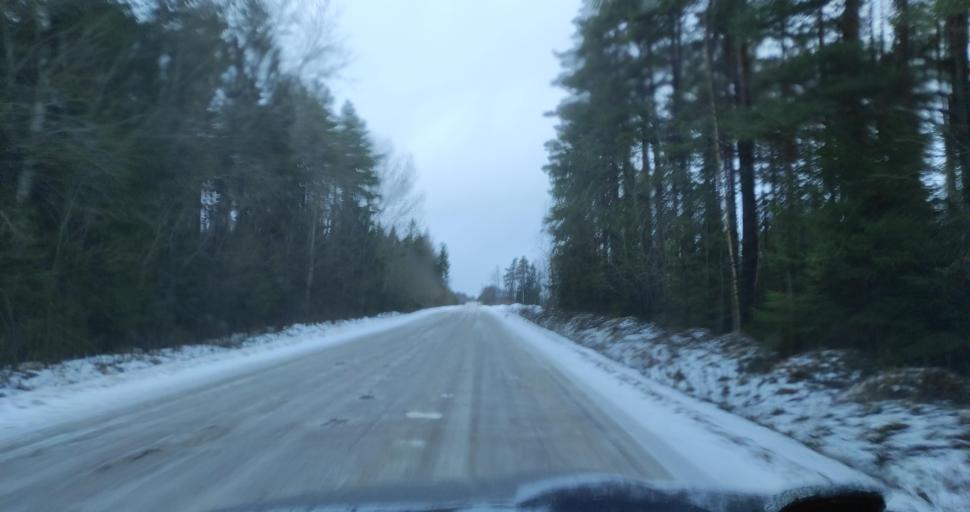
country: LV
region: Dundaga
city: Dundaga
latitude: 57.4927
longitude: 22.0202
